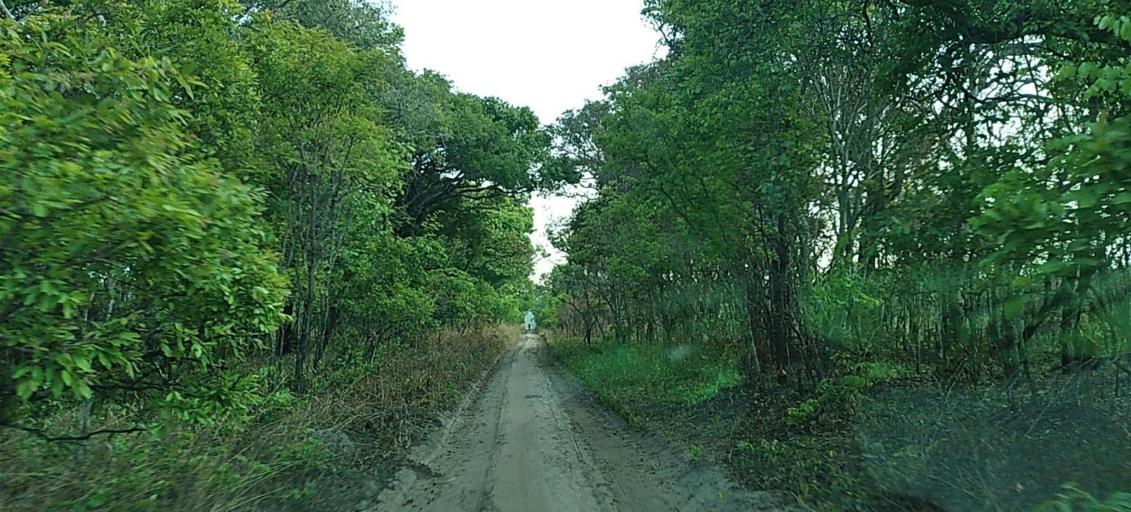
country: ZM
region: North-Western
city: Mwinilunga
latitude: -11.3232
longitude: 24.7385
